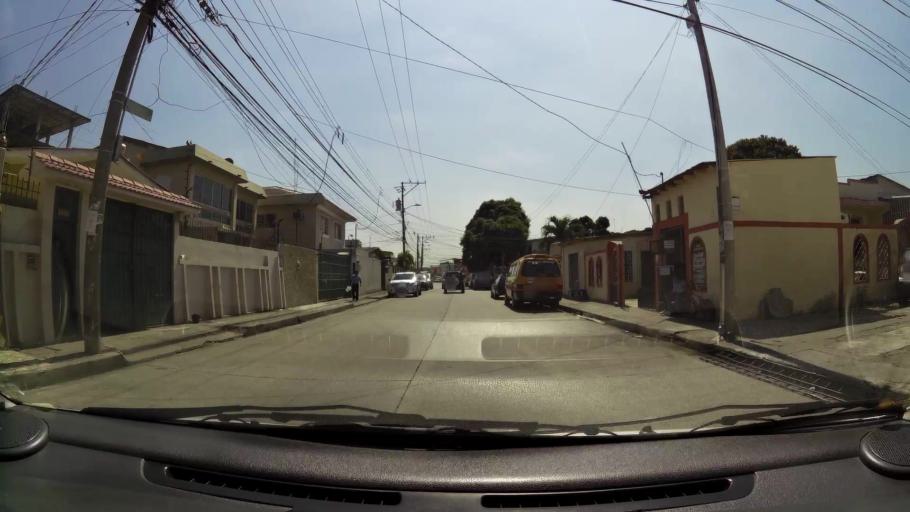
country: EC
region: Guayas
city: Guayaquil
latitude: -2.1625
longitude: -79.9133
